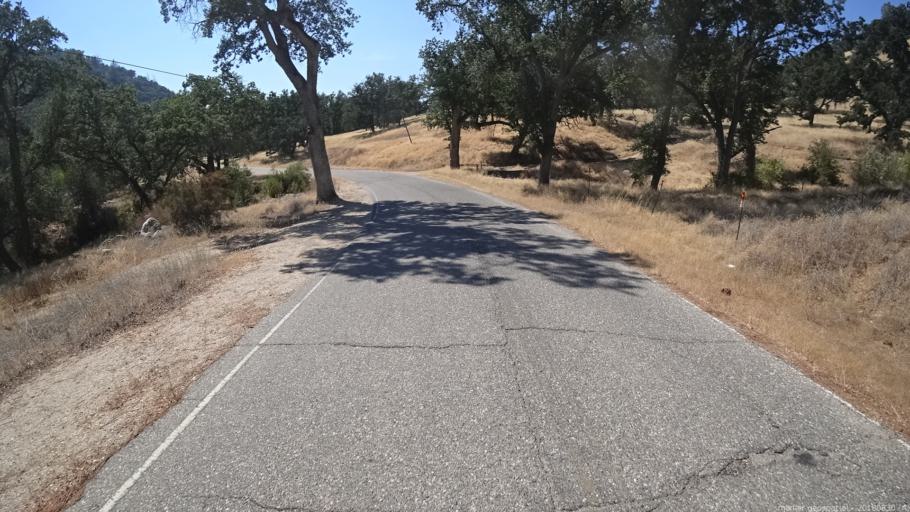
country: US
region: California
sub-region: Monterey County
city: King City
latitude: 36.0734
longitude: -121.3582
